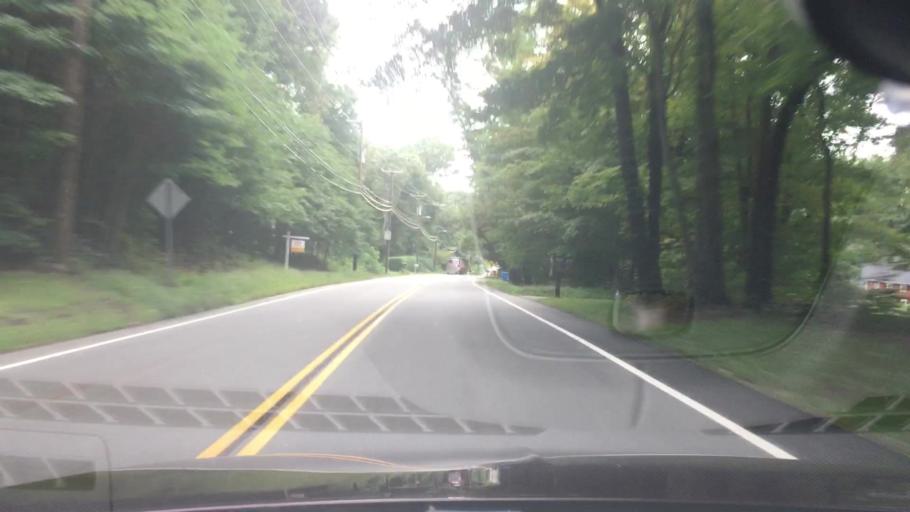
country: US
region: Connecticut
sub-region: New Haven County
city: Madison Center
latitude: 41.2974
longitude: -72.6029
